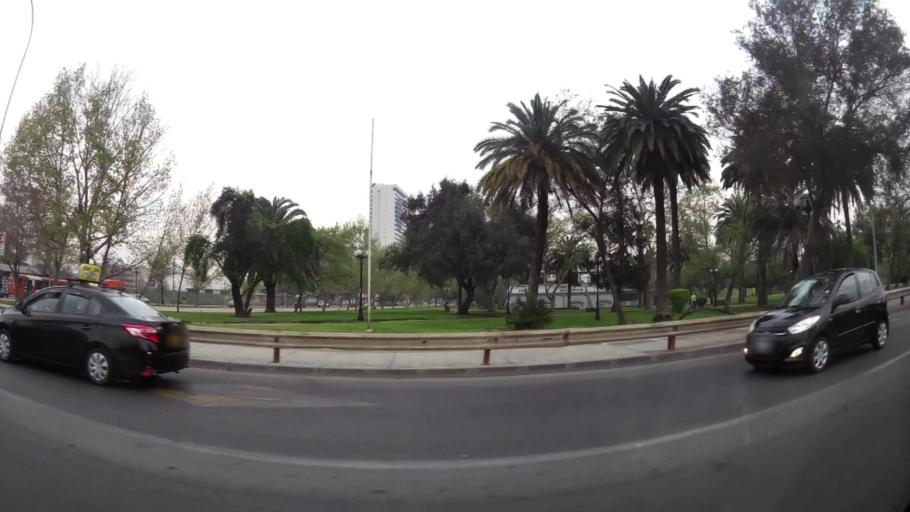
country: CL
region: Santiago Metropolitan
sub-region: Provincia de Santiago
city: Santiago
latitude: -33.4277
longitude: -70.6718
